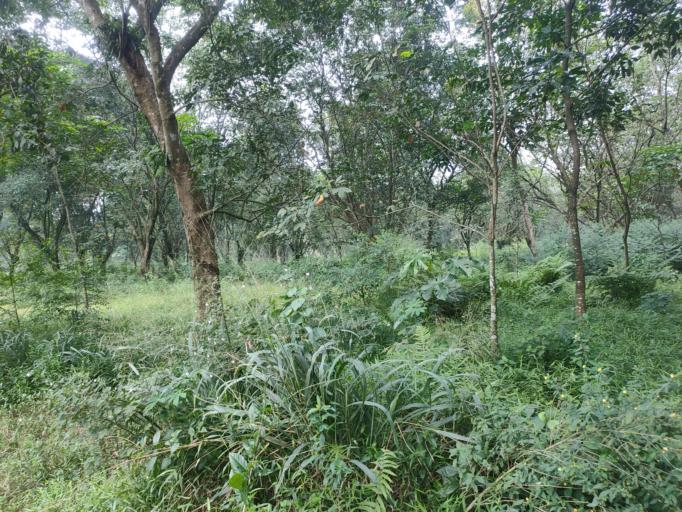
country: ID
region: West Java
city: Ciampea
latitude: -6.5000
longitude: 106.6631
